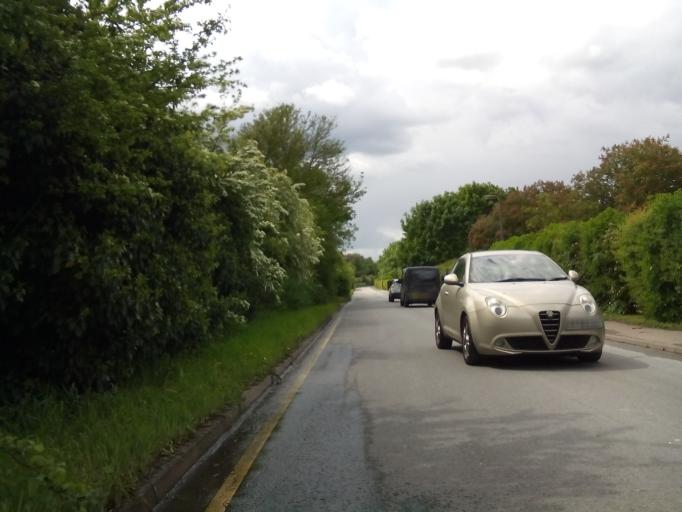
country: GB
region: England
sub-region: Cambridgeshire
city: Fulbourn
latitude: 52.1848
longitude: 0.2022
